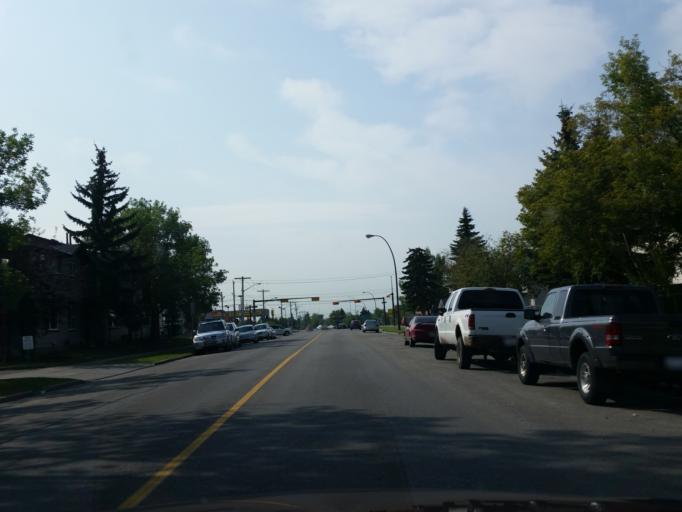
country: CA
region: Alberta
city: Calgary
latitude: 51.0703
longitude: -114.0134
